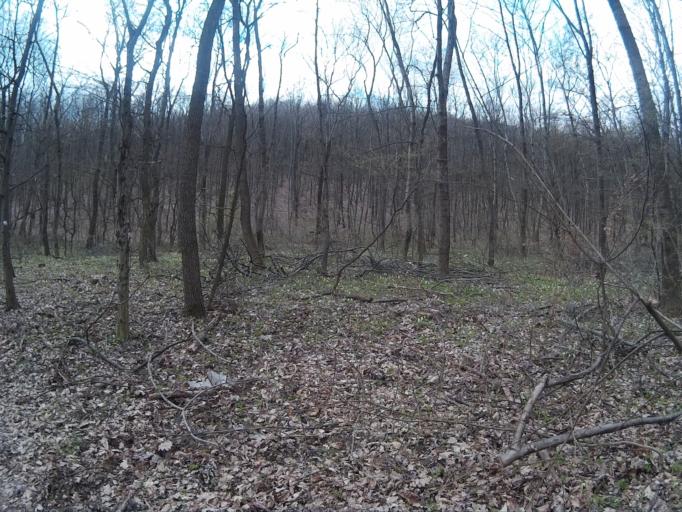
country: HU
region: Pest
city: Kosd
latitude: 47.8306
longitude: 19.1746
